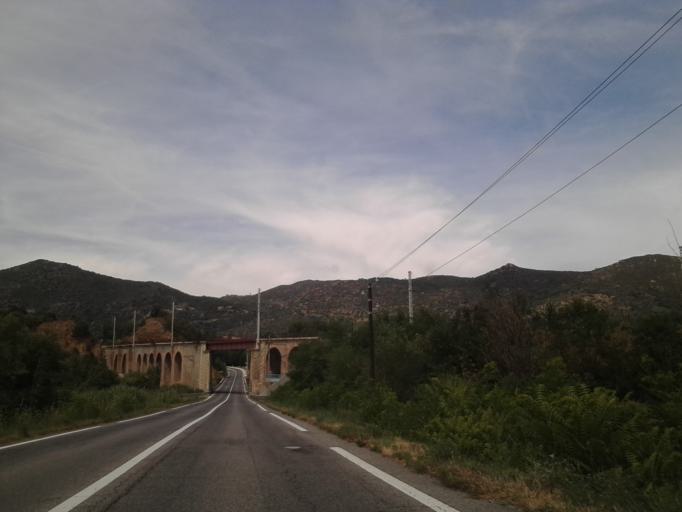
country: FR
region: Languedoc-Roussillon
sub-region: Departement des Pyrenees-Orientales
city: Vinca
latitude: 42.6484
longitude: 2.5571
